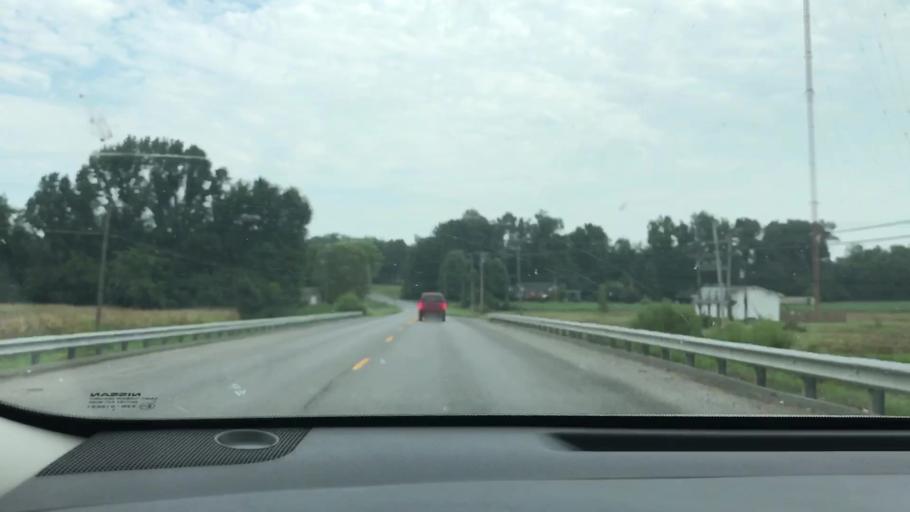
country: US
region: Kentucky
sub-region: Calloway County
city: Murray
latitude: 36.6271
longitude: -88.3019
